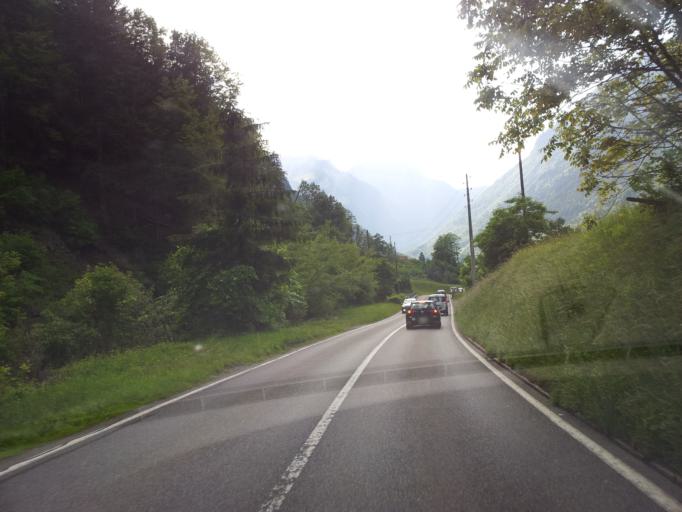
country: CH
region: Bern
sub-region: Interlaken-Oberhasli District
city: Lauterbrunnen
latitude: 46.6362
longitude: 7.9598
